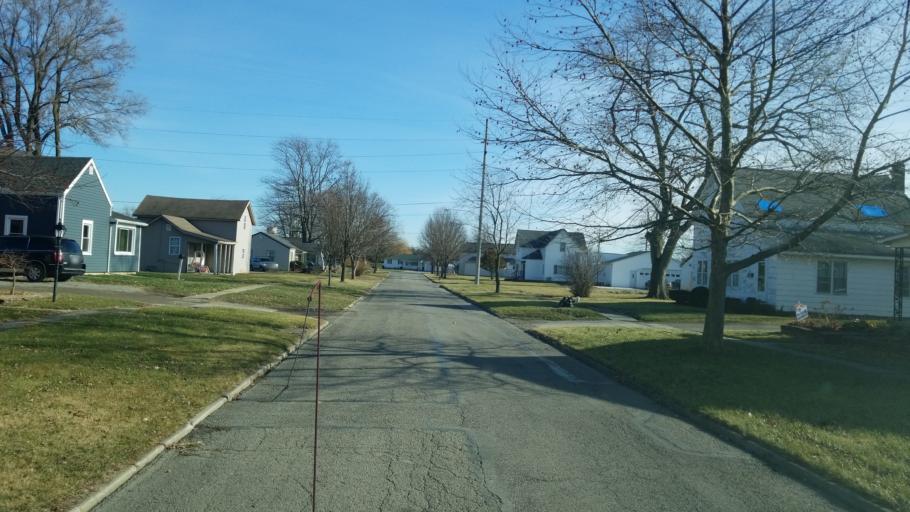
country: US
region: Ohio
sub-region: Putnam County
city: Leipsic
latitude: 41.1023
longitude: -83.9838
